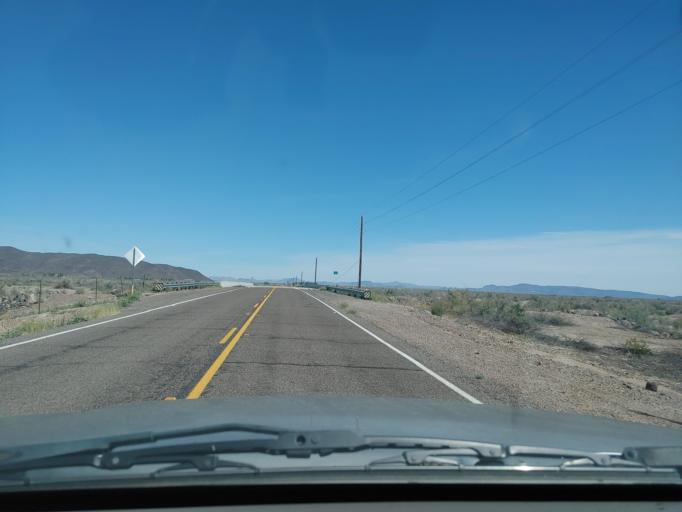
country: US
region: Arizona
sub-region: Maricopa County
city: Gila Bend
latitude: 32.9612
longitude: -113.3059
